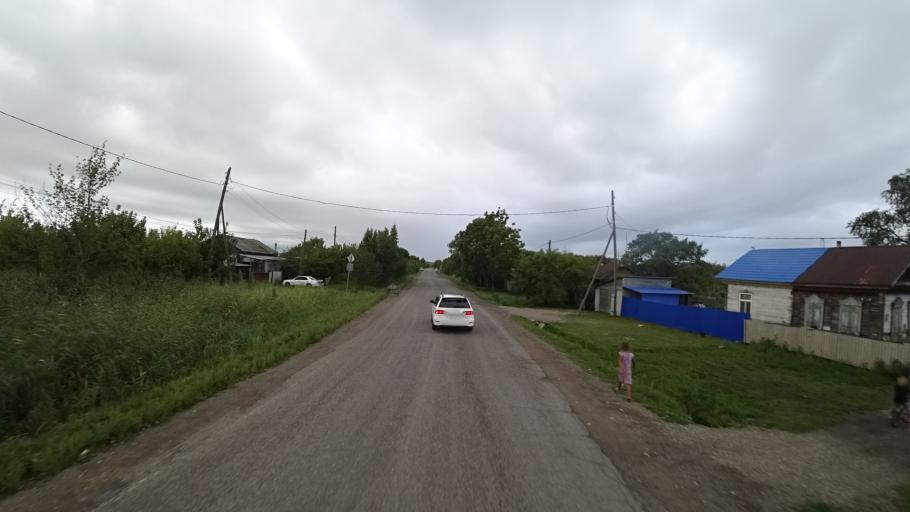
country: RU
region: Primorskiy
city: Chernigovka
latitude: 44.3516
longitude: 132.5693
